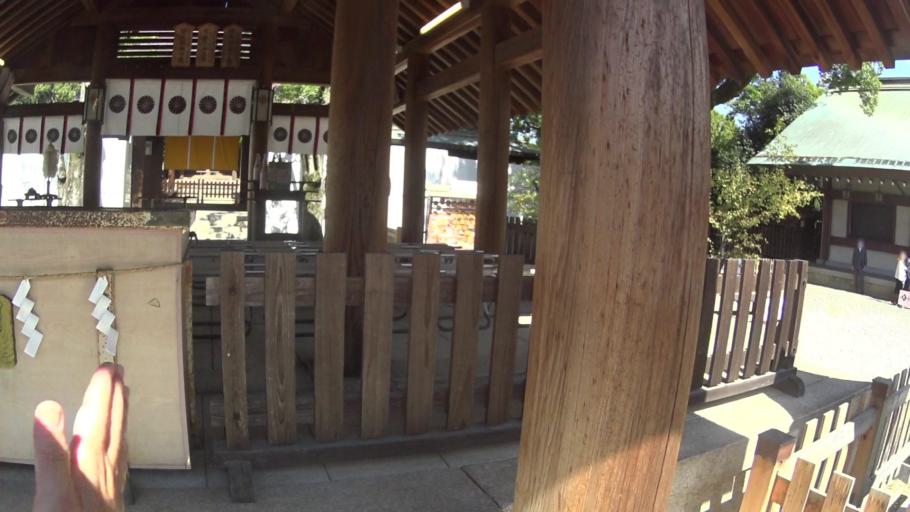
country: JP
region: Osaka
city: Kishiwada
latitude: 34.4764
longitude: 135.3777
